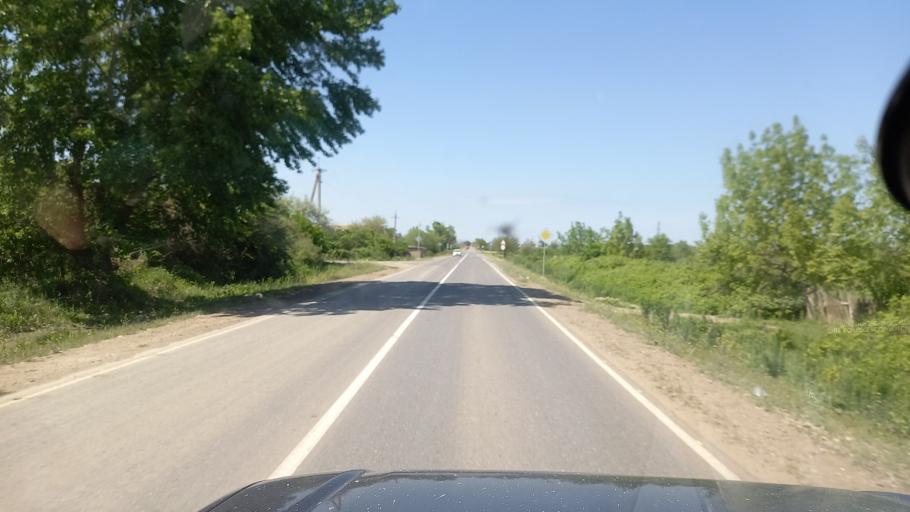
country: RU
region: Dagestan
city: Novaya Maka
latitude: 41.8169
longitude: 48.4026
